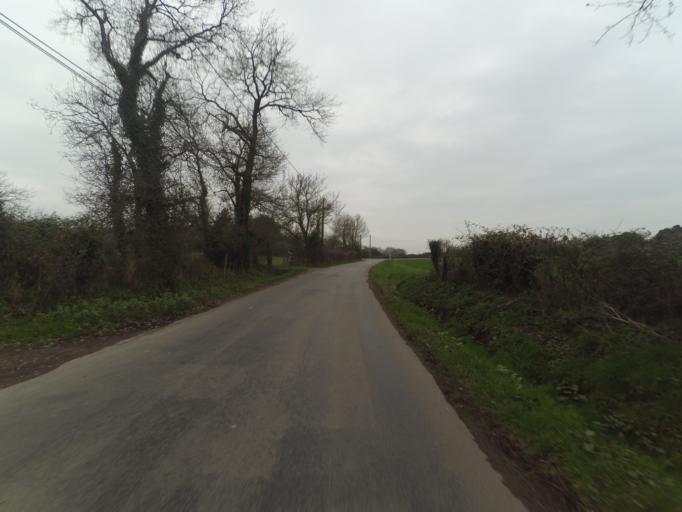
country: FR
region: Pays de la Loire
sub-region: Departement de la Loire-Atlantique
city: Sautron
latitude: 47.2528
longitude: -1.7075
